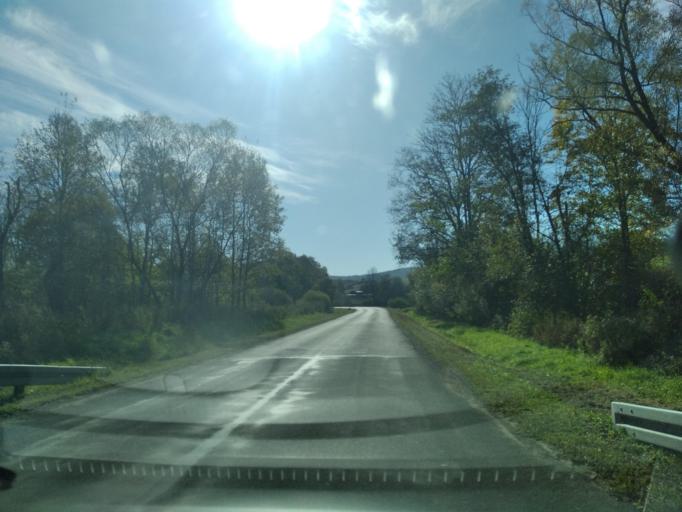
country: PL
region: Subcarpathian Voivodeship
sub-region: Powiat sanocki
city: Komancza
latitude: 49.4082
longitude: 21.9788
